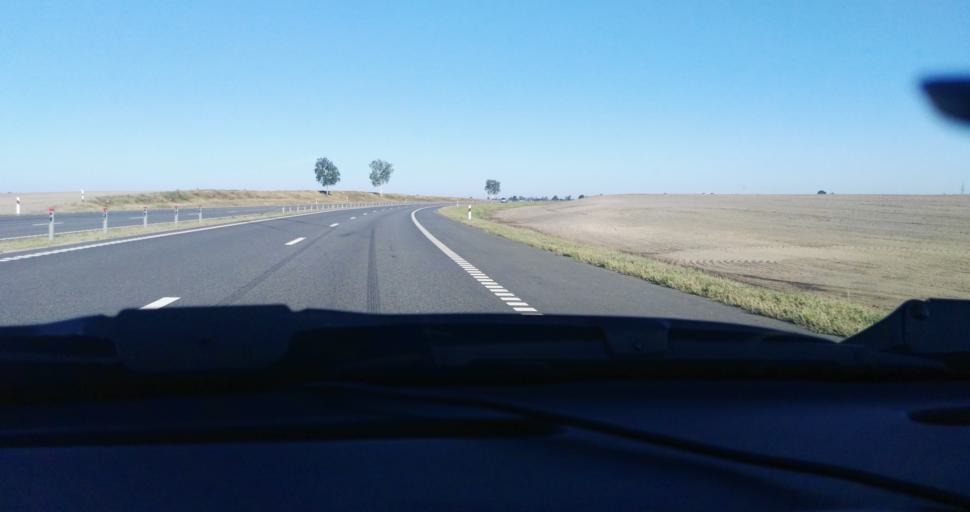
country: BY
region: Gomel
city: Buda-Kashalyova
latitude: 52.5075
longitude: 30.6363
